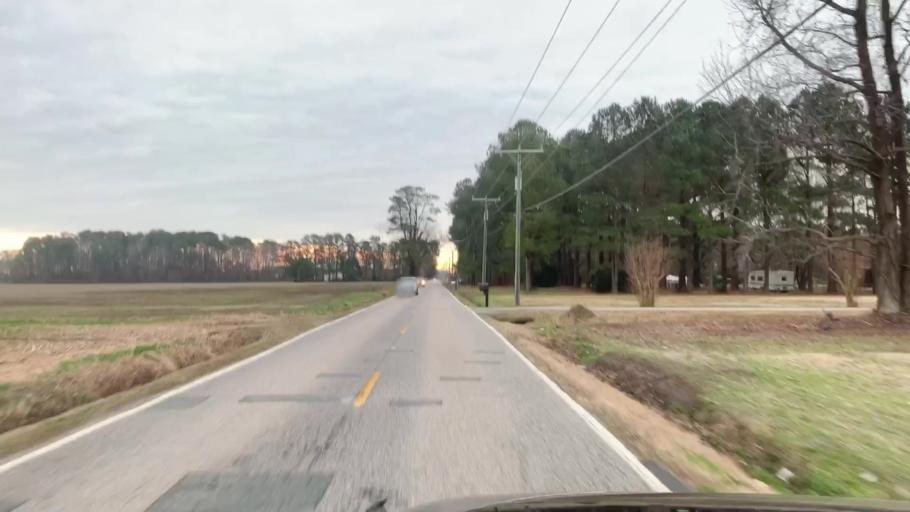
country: US
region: North Carolina
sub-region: Currituck County
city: Moyock
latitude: 36.6324
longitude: -76.1814
